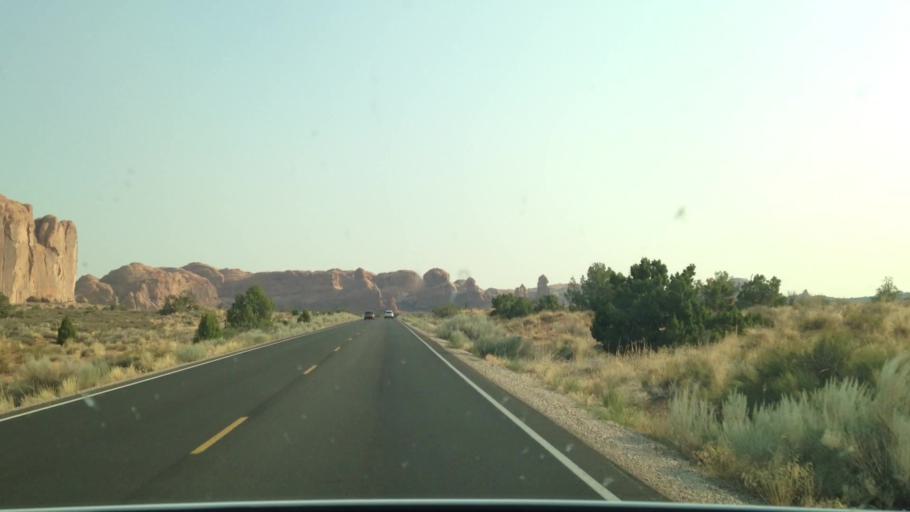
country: US
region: Utah
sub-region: Grand County
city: Moab
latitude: 38.6738
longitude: -109.5877
